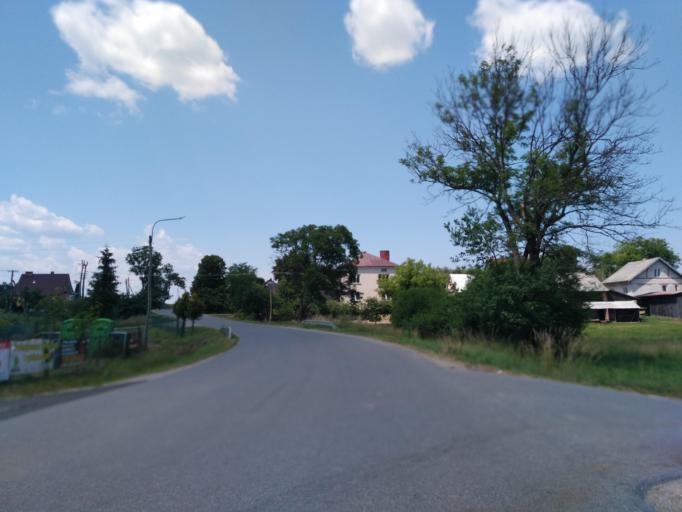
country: PL
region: Subcarpathian Voivodeship
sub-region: Powiat sanocki
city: Niebieszczany
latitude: 49.4919
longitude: 22.1778
